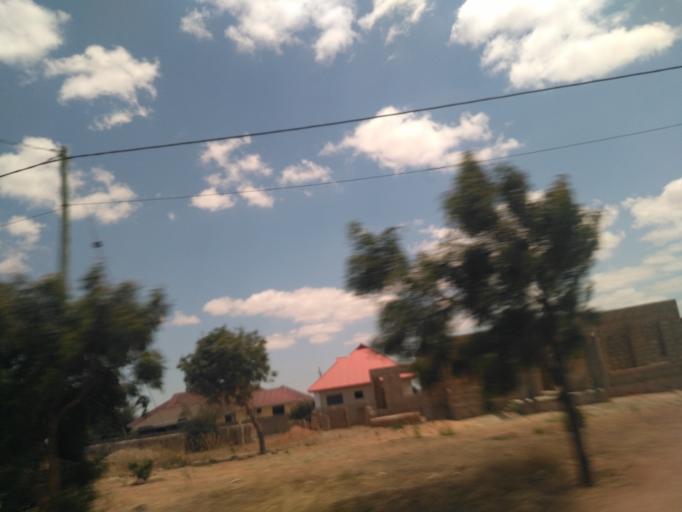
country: TZ
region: Dodoma
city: Kisasa
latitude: -6.1777
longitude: 35.7883
